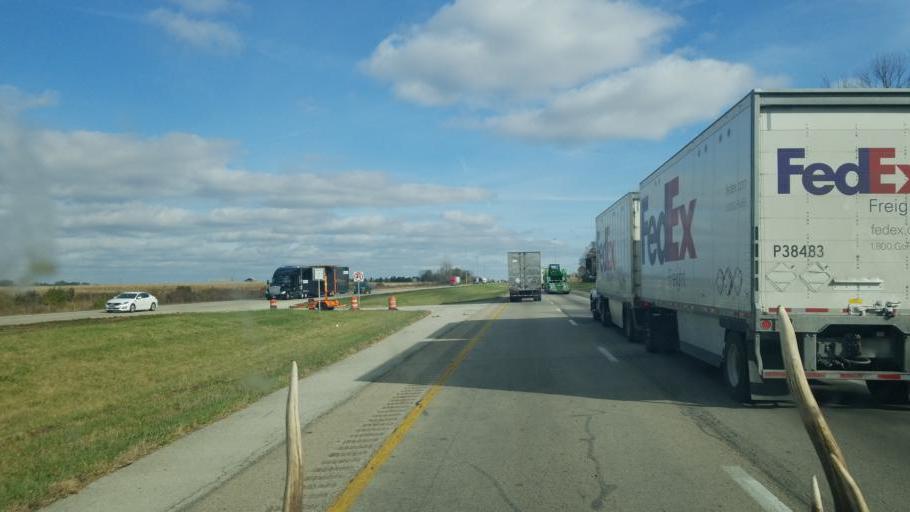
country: US
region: Ohio
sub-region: Preble County
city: New Paris
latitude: 39.8284
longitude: -84.7742
